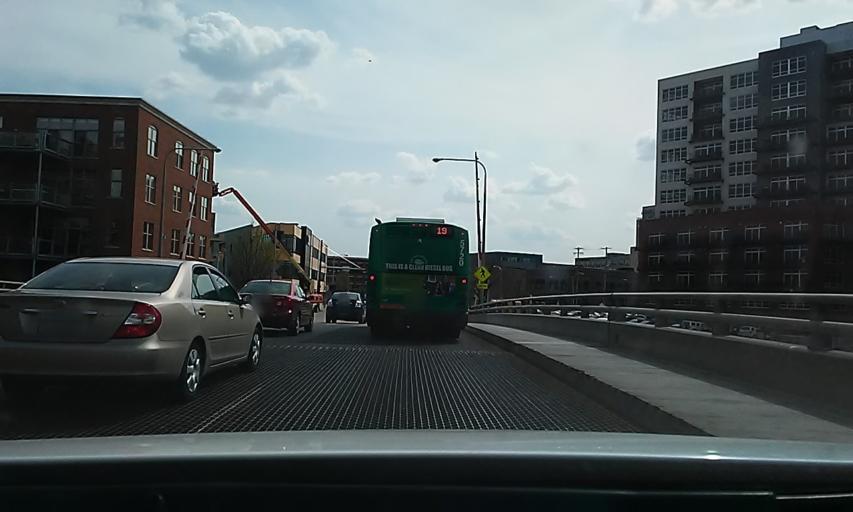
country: US
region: Wisconsin
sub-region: Milwaukee County
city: Milwaukee
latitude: 43.0314
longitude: -87.9100
